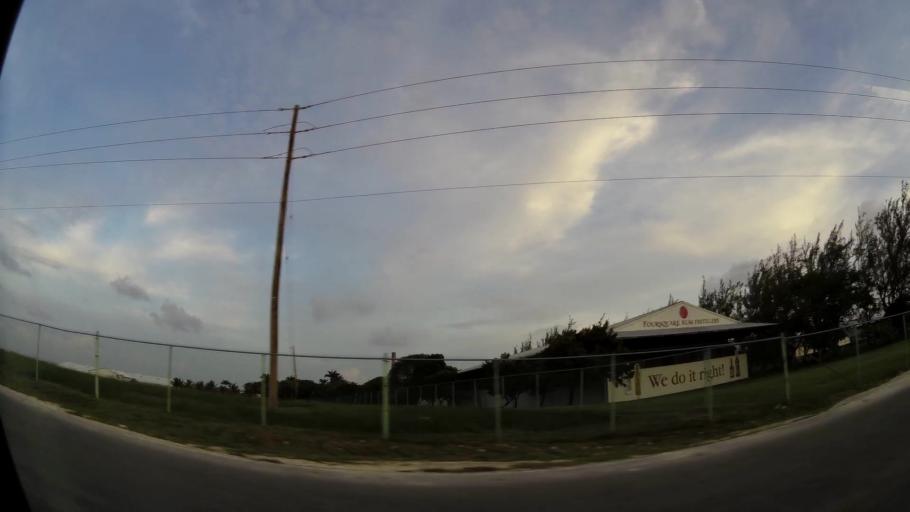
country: BB
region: Saint Philip
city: Crane
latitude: 13.1062
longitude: -59.4851
